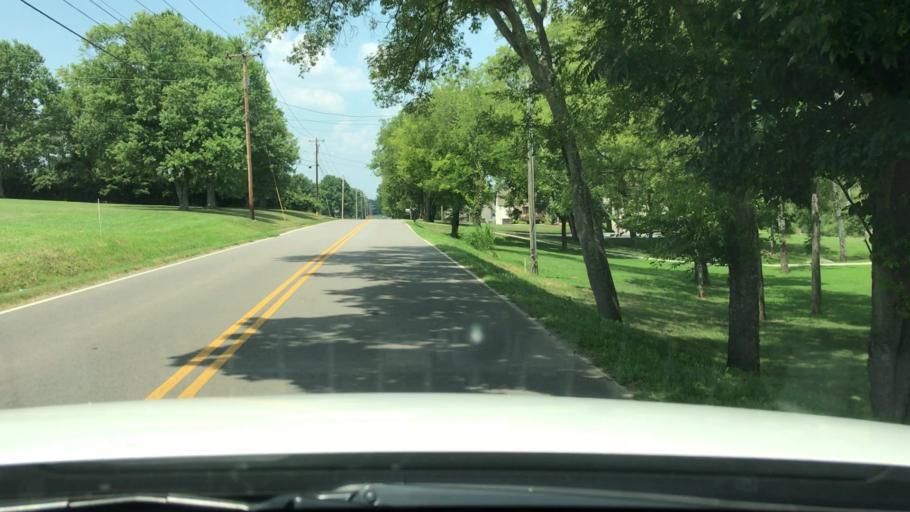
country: US
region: Tennessee
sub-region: Sumner County
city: Gallatin
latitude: 36.3595
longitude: -86.4499
